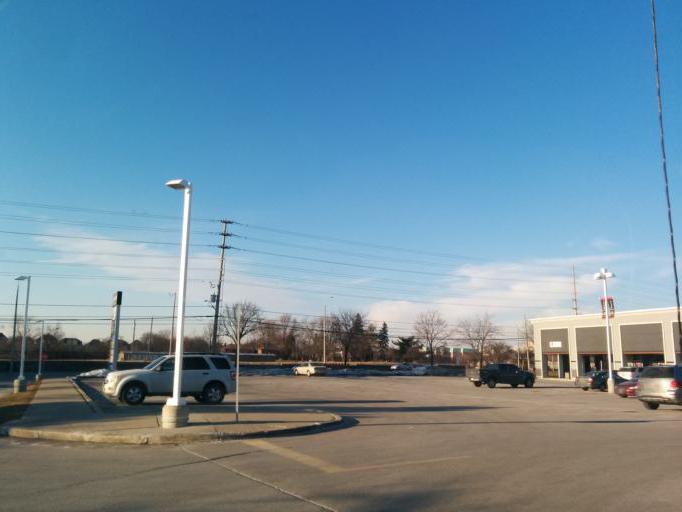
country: CA
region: Ontario
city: Mississauga
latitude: 43.6077
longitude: -79.6506
